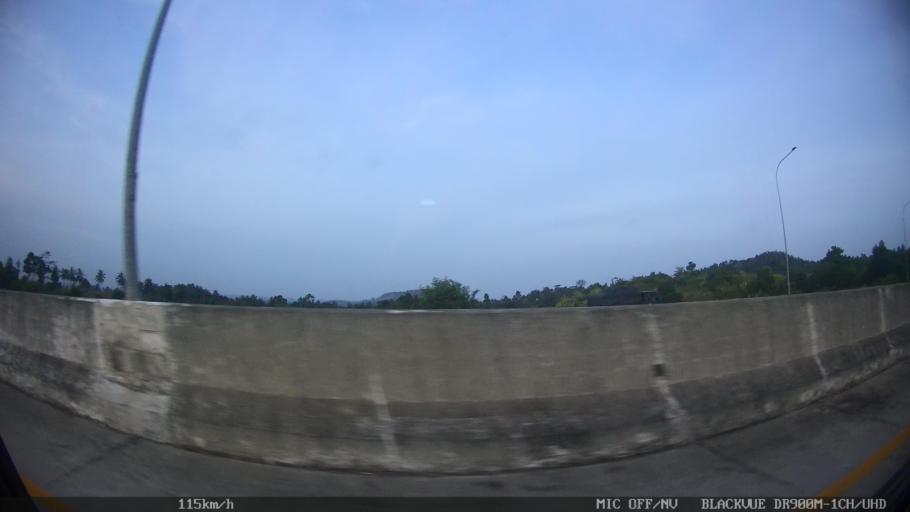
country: ID
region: Lampung
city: Penengahan
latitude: -5.8030
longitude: 105.7311
